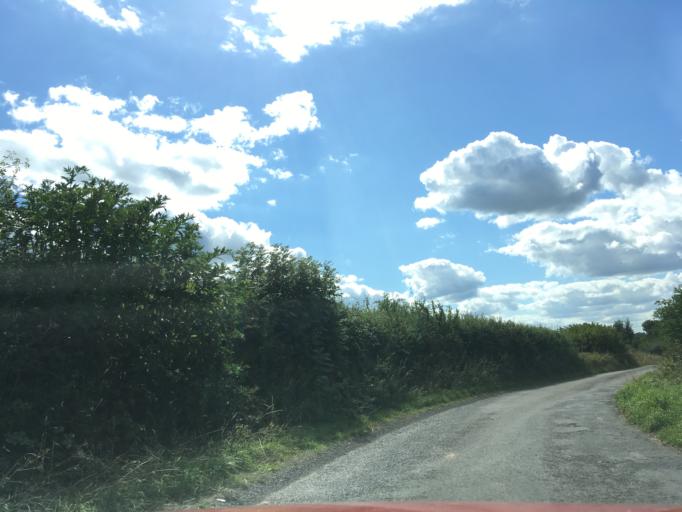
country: IE
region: Munster
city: Cashel
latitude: 52.4840
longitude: -7.9661
